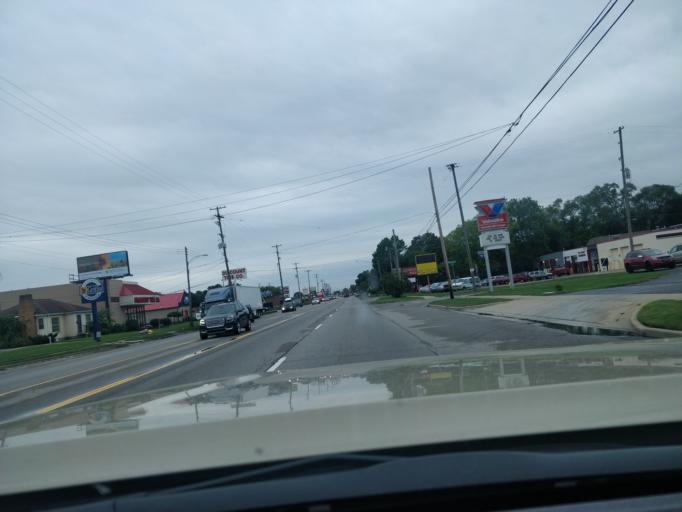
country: US
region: Michigan
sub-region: Kent County
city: Wyoming
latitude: 42.9138
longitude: -85.7177
